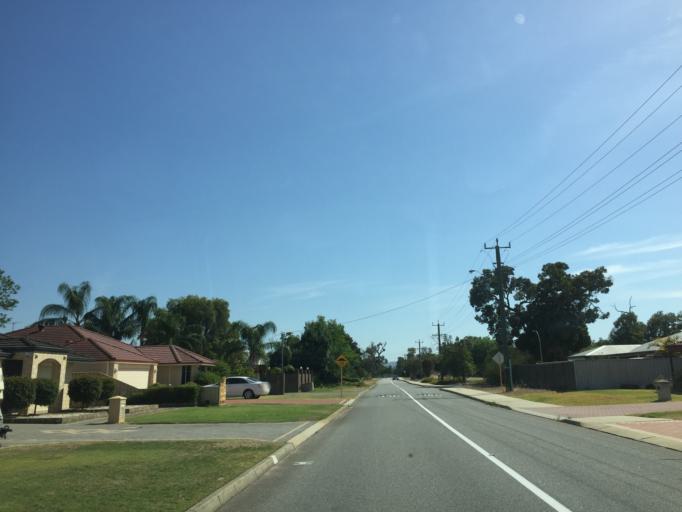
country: AU
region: Western Australia
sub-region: Gosnells
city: Southern River
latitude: -32.0840
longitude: 115.9582
